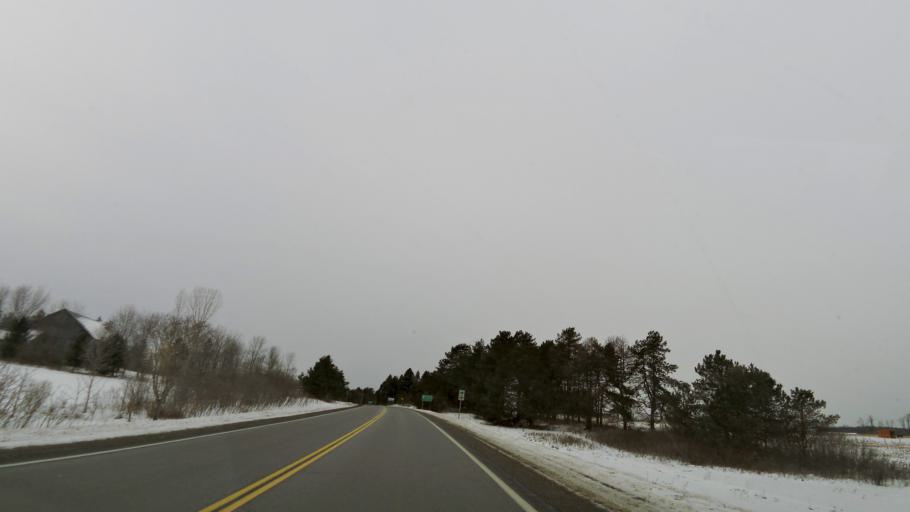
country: CA
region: Ontario
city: Cambridge
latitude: 43.3268
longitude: -80.2051
